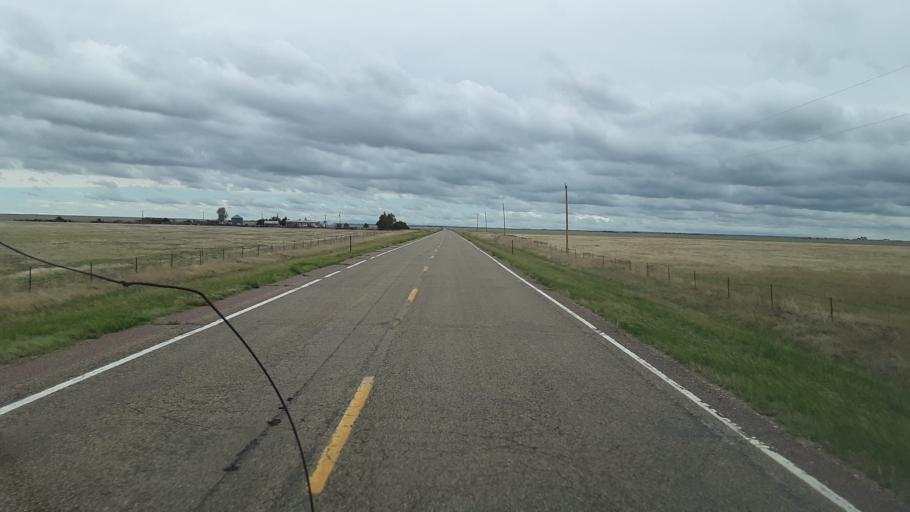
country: US
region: Colorado
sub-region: Lincoln County
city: Limon
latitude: 38.8388
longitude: -103.8838
